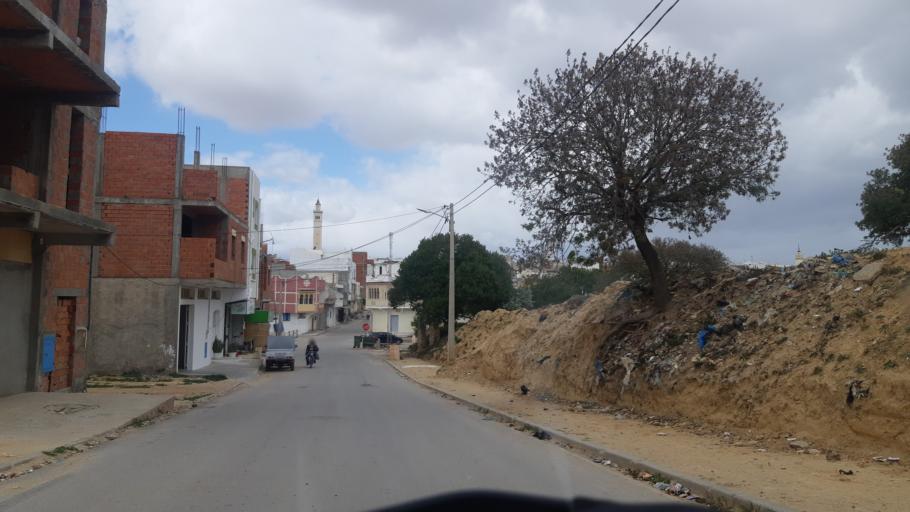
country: TN
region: Susah
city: Akouda
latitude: 35.8666
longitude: 10.5366
